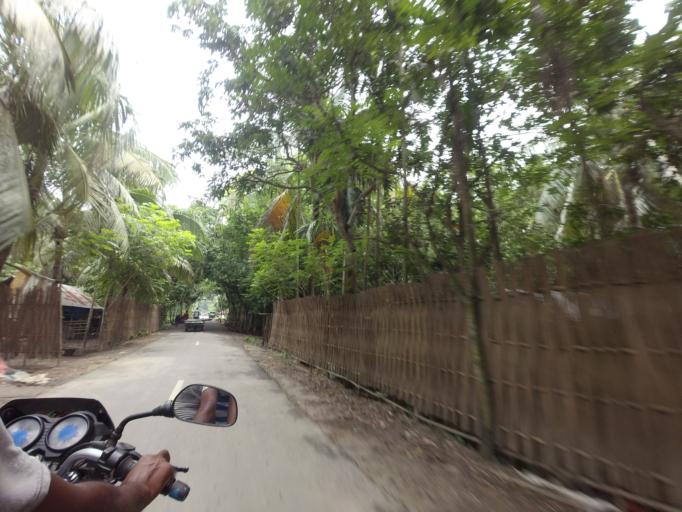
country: BD
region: Khulna
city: Kalia
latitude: 23.1021
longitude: 89.6482
